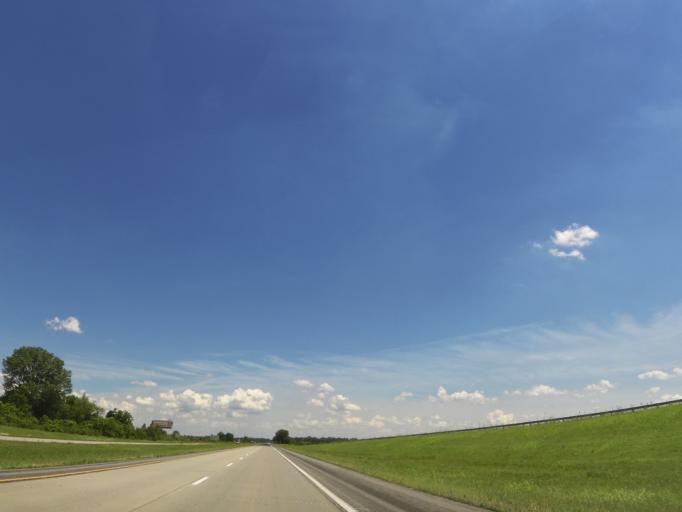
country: US
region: Missouri
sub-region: Pemiscot County
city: Caruthersville
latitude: 36.1512
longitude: -89.6631
